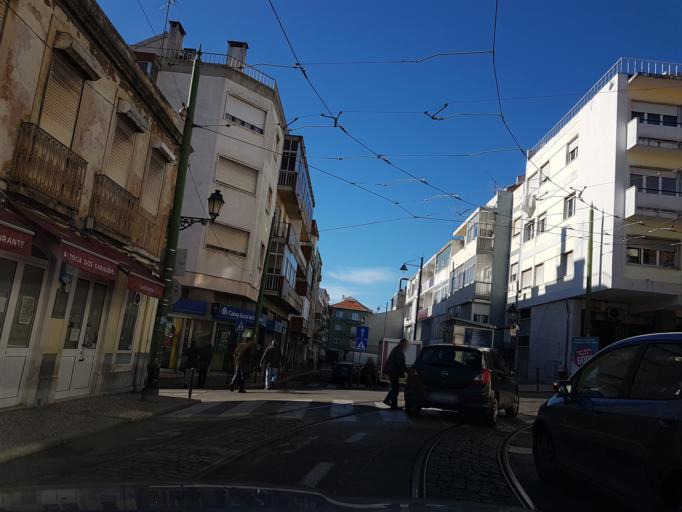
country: PT
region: Lisbon
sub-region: Oeiras
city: Alges
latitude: 38.7036
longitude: -9.1954
